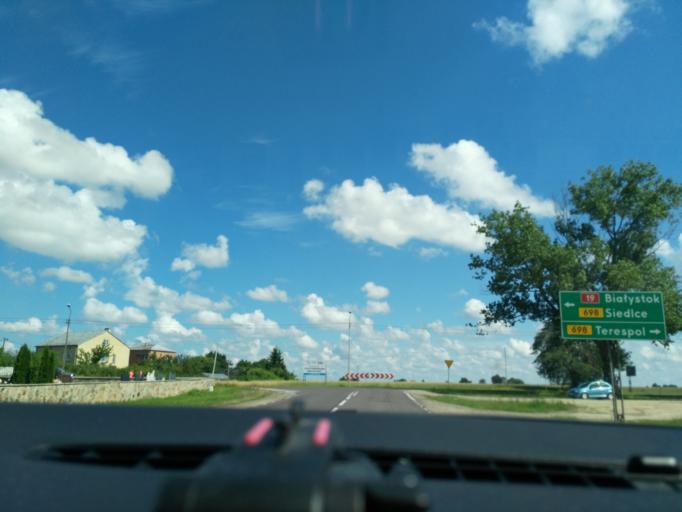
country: PL
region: Masovian Voivodeship
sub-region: Powiat losicki
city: Losice
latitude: 52.2101
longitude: 22.7310
